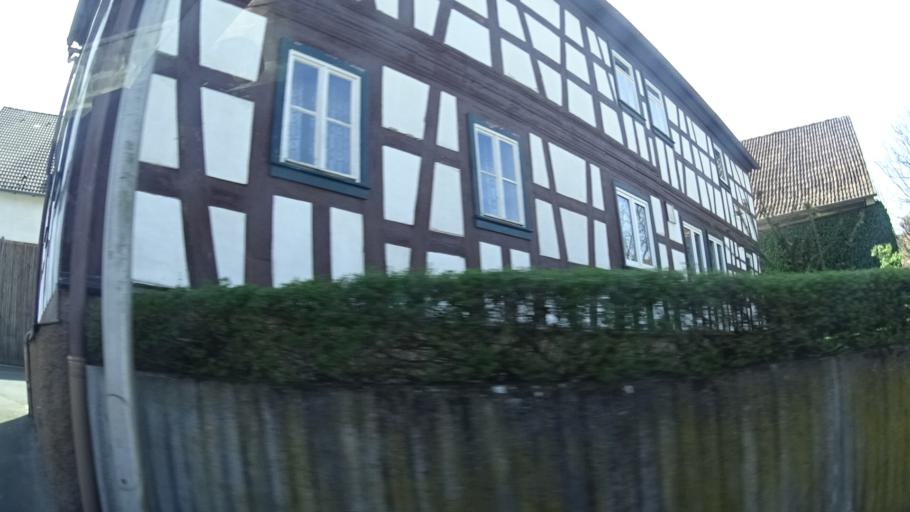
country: DE
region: Bavaria
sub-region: Regierungsbezirk Unterfranken
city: Burgpreppach
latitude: 50.1684
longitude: 10.6348
